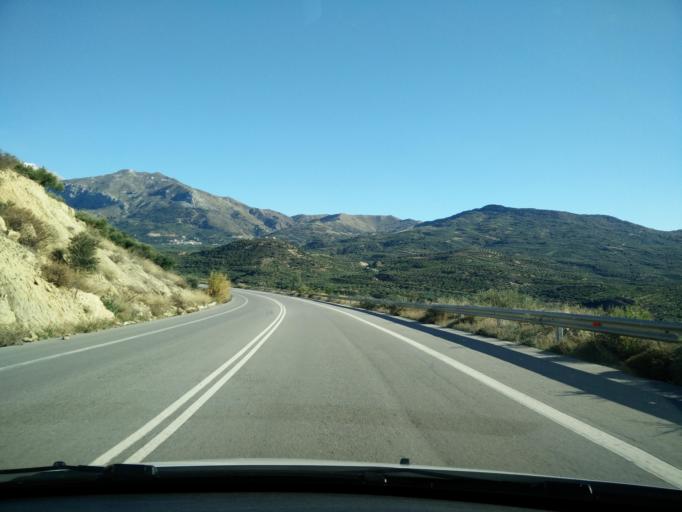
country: GR
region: Crete
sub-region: Nomos Irakleiou
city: Arkalochori
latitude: 35.0807
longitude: 25.3173
